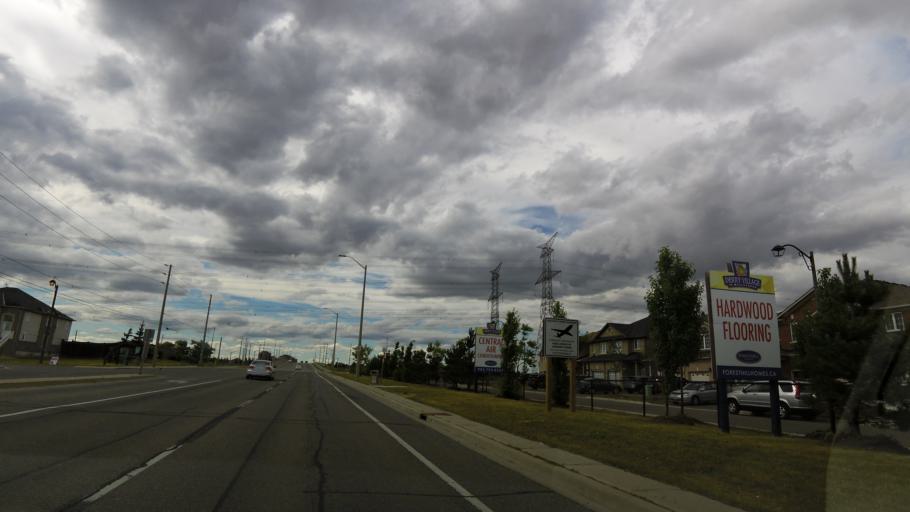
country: CA
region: Ontario
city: Brampton
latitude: 43.6428
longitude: -79.7252
